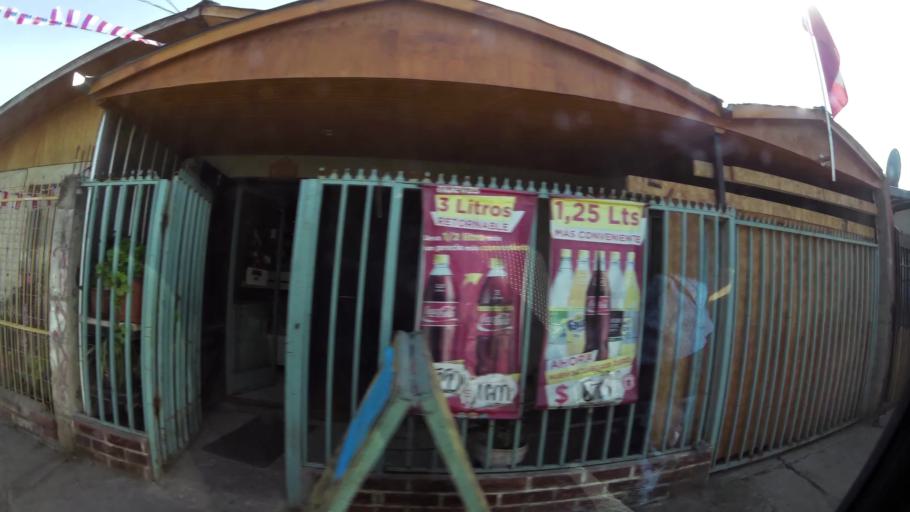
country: CL
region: Santiago Metropolitan
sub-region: Provincia de Santiago
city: Lo Prado
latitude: -33.4187
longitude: -70.7621
